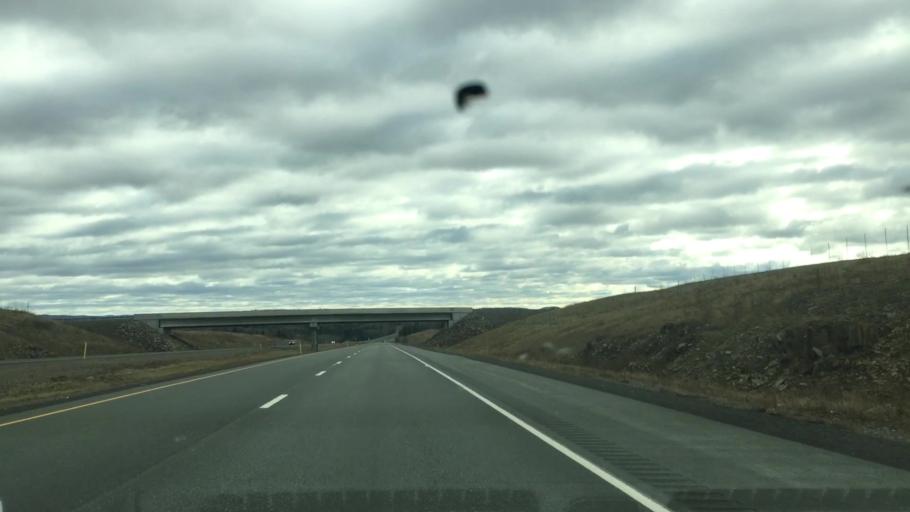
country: CA
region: New Brunswick
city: Florenceville-Bristol
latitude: 46.5486
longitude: -67.7298
